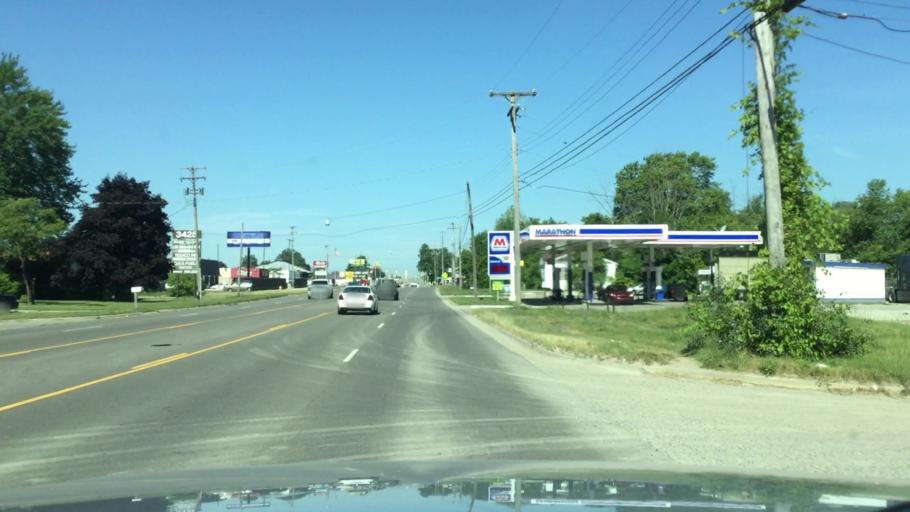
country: US
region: Michigan
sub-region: Genesee County
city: Beecher
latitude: 43.0608
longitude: -83.7482
